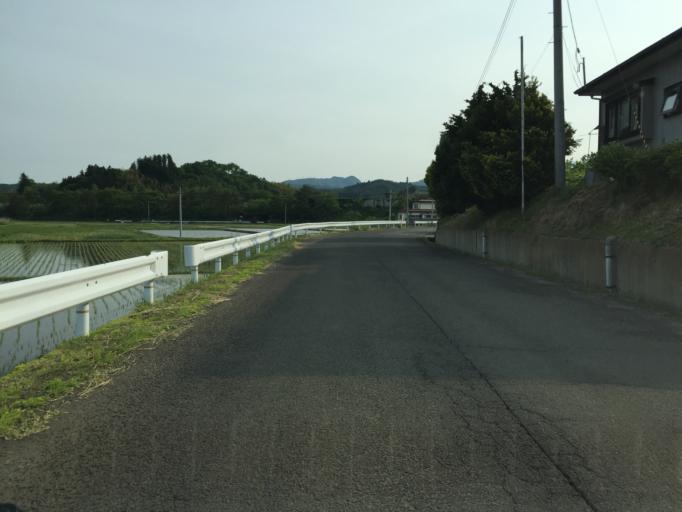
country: JP
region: Fukushima
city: Fukushima-shi
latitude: 37.7213
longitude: 140.4333
